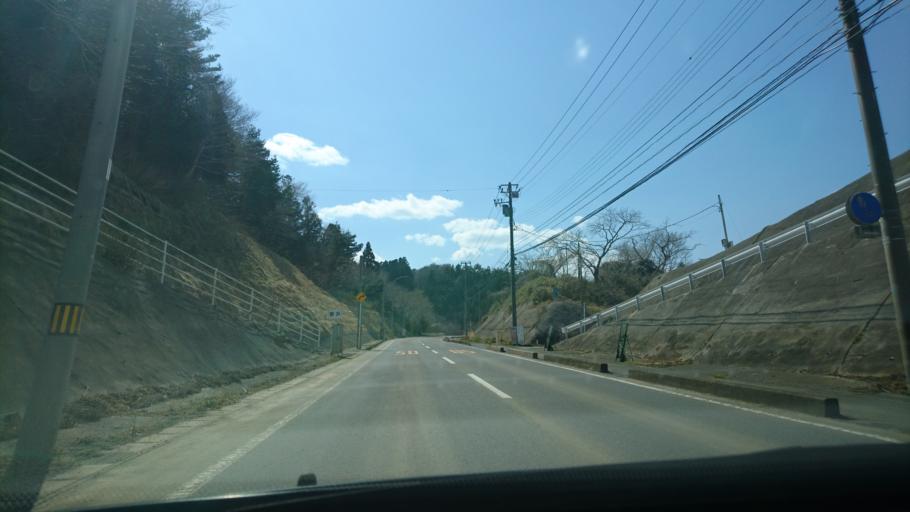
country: JP
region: Miyagi
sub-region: Oshika Gun
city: Onagawa Cho
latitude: 38.6367
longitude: 141.5074
